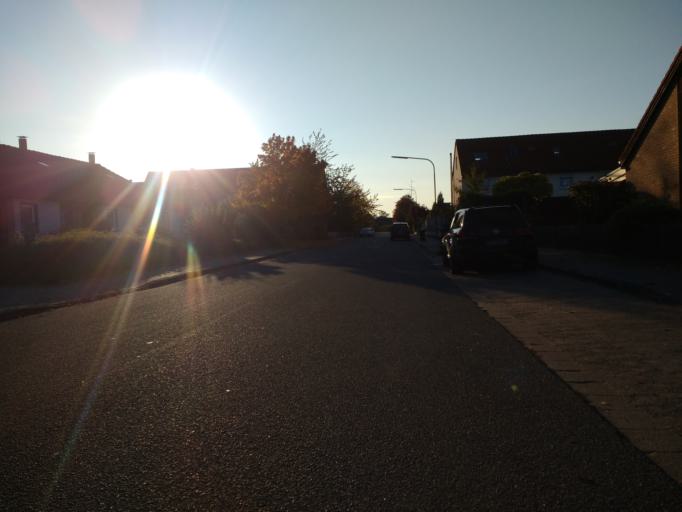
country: DE
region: Lower Saxony
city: Gifhorn
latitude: 52.4870
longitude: 10.5667
